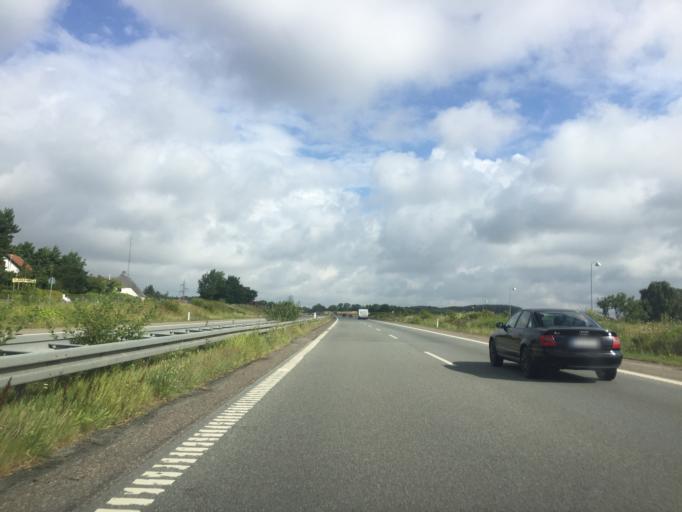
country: DK
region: South Denmark
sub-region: Svendborg Kommune
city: Svendborg
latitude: 55.0827
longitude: 10.5735
